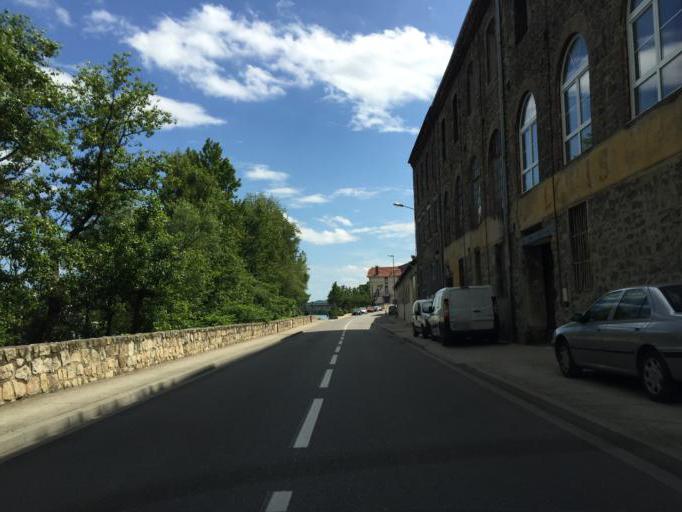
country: FR
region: Rhone-Alpes
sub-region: Departement de l'Ardeche
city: Andance
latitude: 45.2457
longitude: 4.8004
